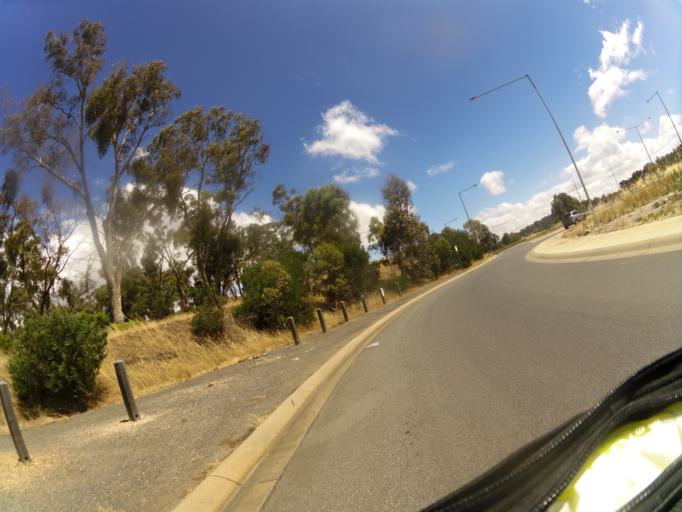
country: AU
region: Victoria
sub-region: Mount Alexander
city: Castlemaine
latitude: -37.0032
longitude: 144.2508
